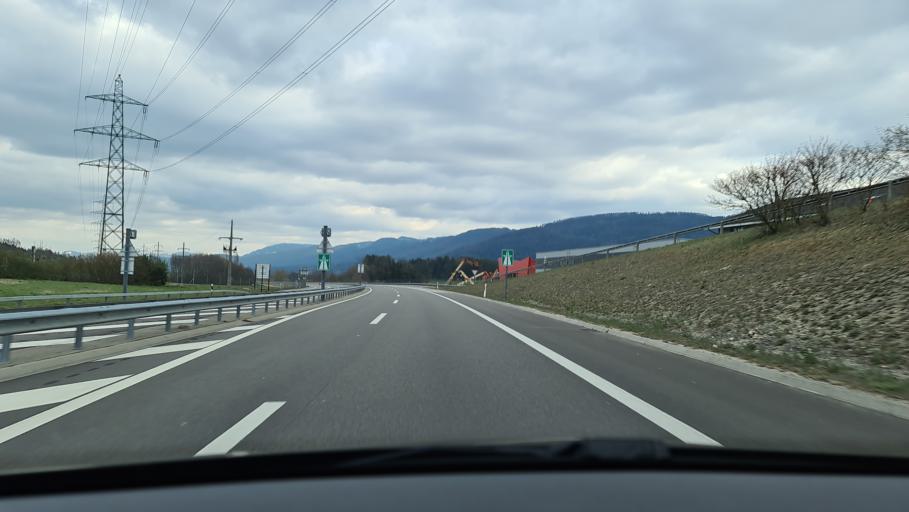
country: CH
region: Jura
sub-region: Delemont District
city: Glovelier
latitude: 47.3422
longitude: 7.2108
